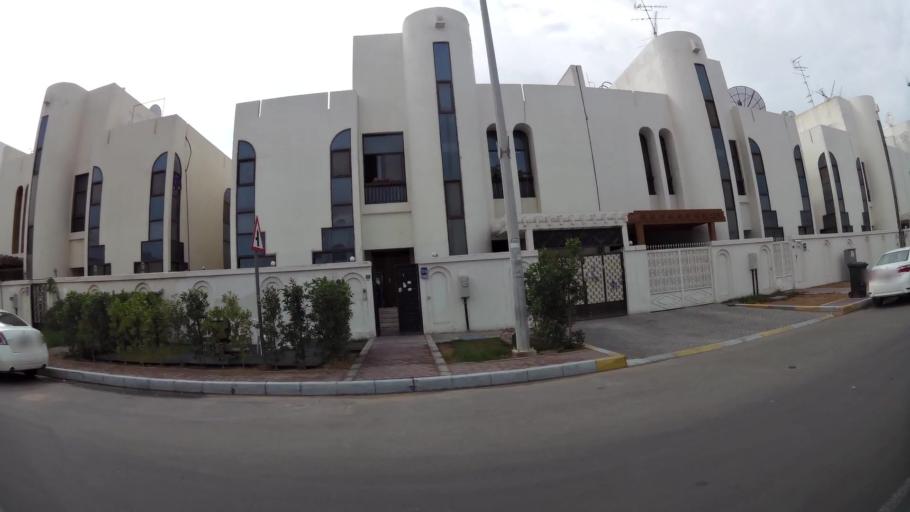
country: AE
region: Abu Dhabi
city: Abu Dhabi
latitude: 24.4393
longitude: 54.4362
